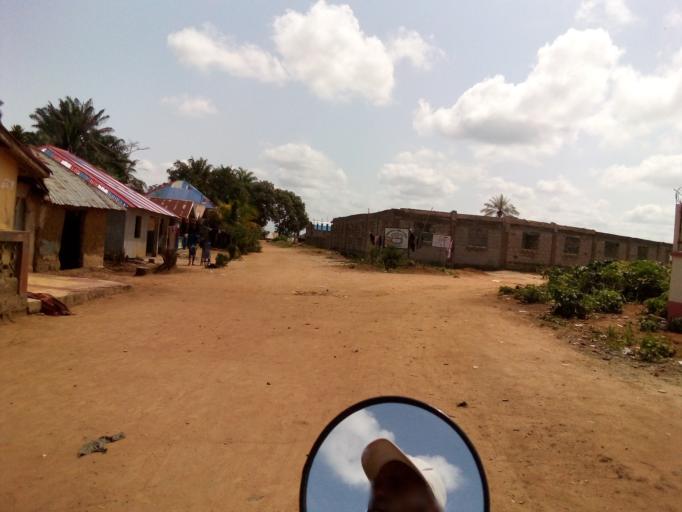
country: SL
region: Western Area
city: Waterloo
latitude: 8.3514
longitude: -13.0181
